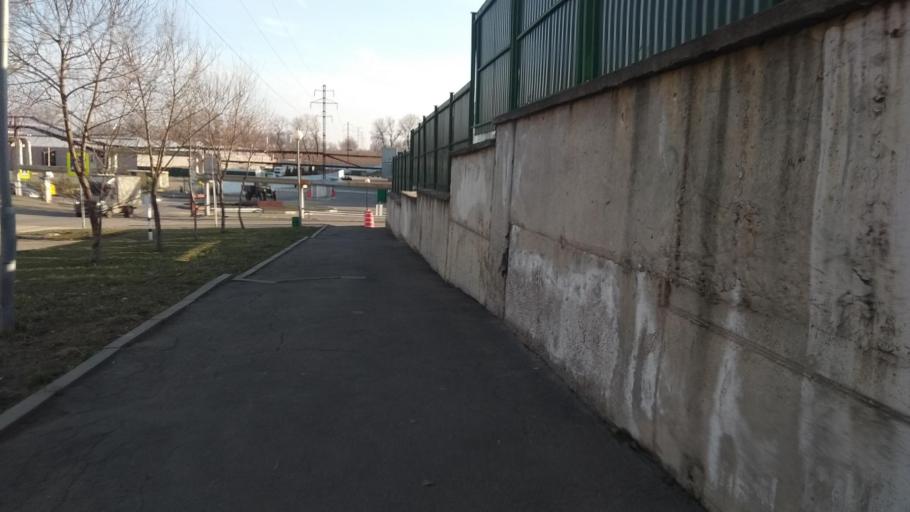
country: RU
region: Moskovskaya
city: Razvilka
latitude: 55.5841
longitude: 37.7270
